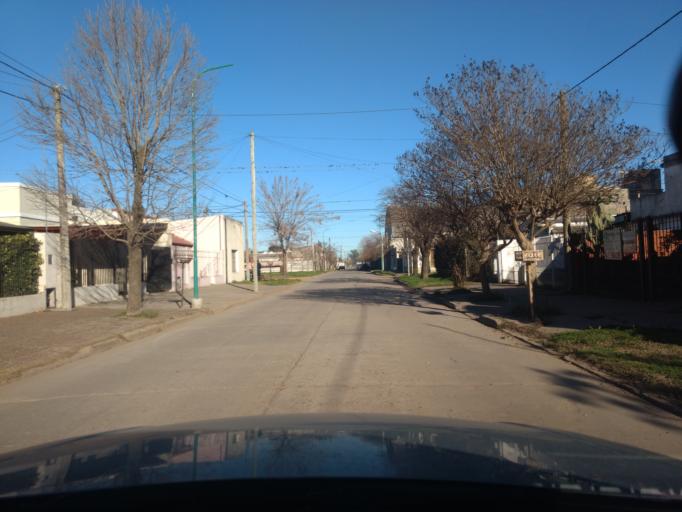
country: AR
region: Buenos Aires
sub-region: Partido de Navarro
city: Navarro
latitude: -35.0009
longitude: -59.2779
